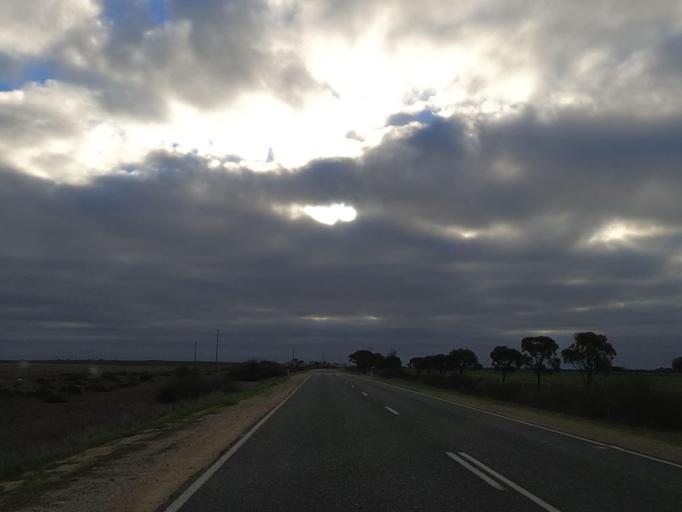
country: AU
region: Victoria
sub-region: Swan Hill
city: Swan Hill
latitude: -35.6487
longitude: 143.8383
